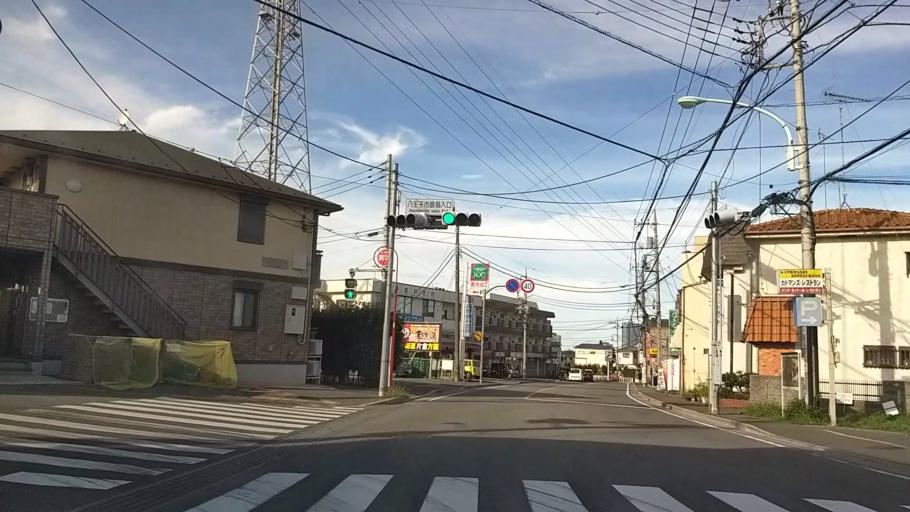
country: JP
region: Tokyo
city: Hachioji
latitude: 35.6428
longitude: 139.3199
